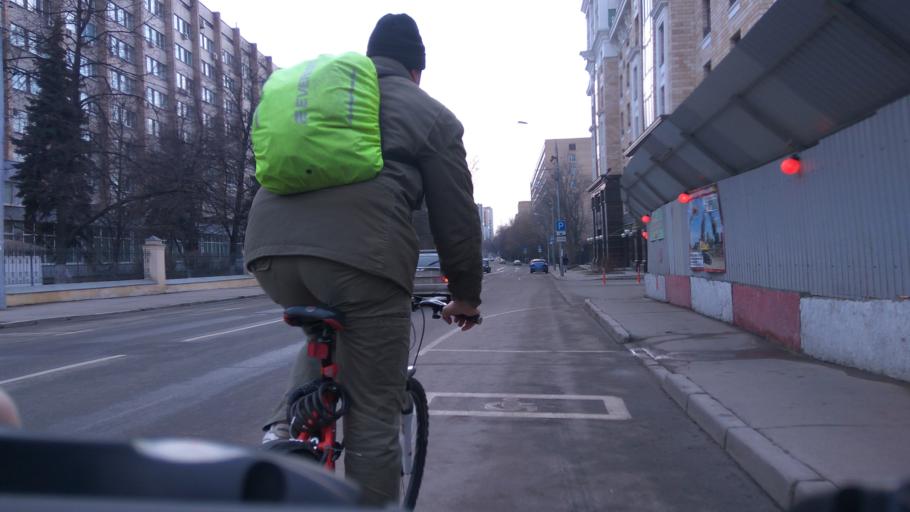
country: RU
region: Moskovskaya
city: Dorogomilovo
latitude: 55.7350
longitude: 37.5726
